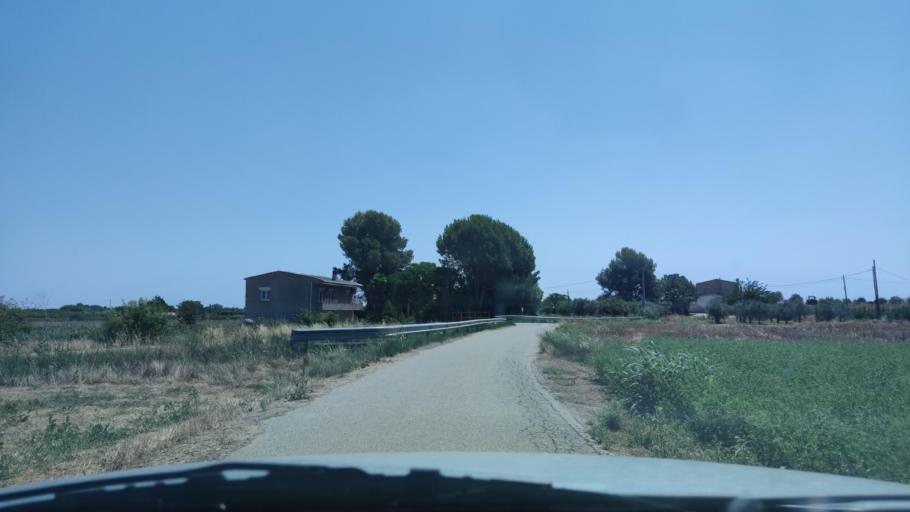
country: ES
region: Catalonia
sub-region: Provincia de Lleida
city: Torrefarrera
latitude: 41.6478
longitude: 0.5890
